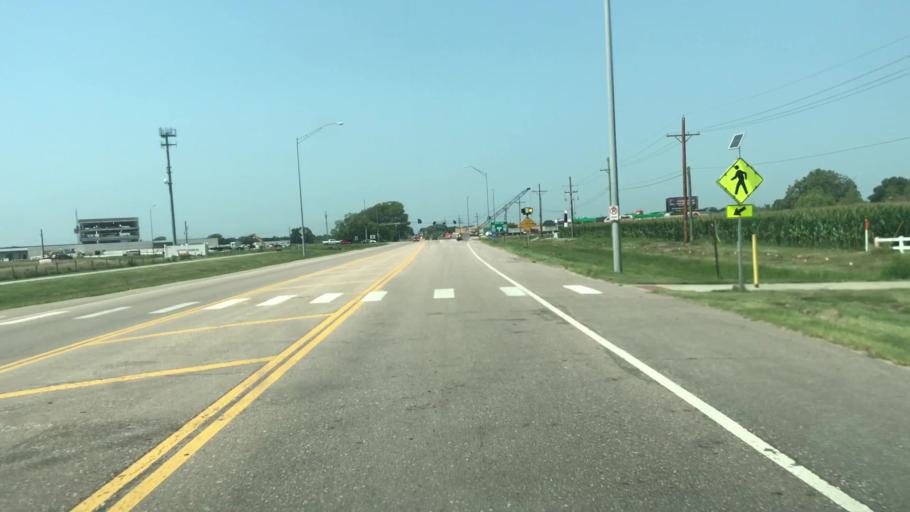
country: US
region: Nebraska
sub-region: Hall County
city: Grand Island
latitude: 40.8880
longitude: -98.3751
